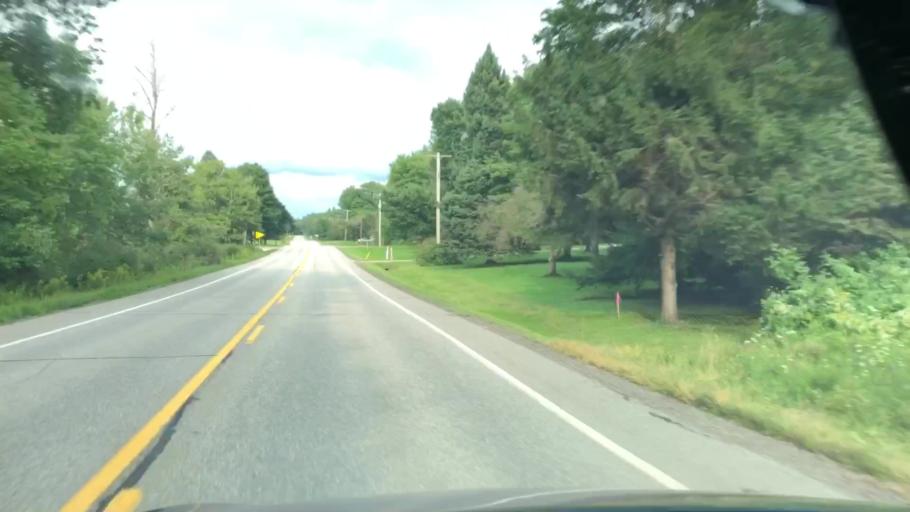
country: US
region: Pennsylvania
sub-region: Erie County
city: Northwest Harborcreek
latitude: 42.0588
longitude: -79.8875
